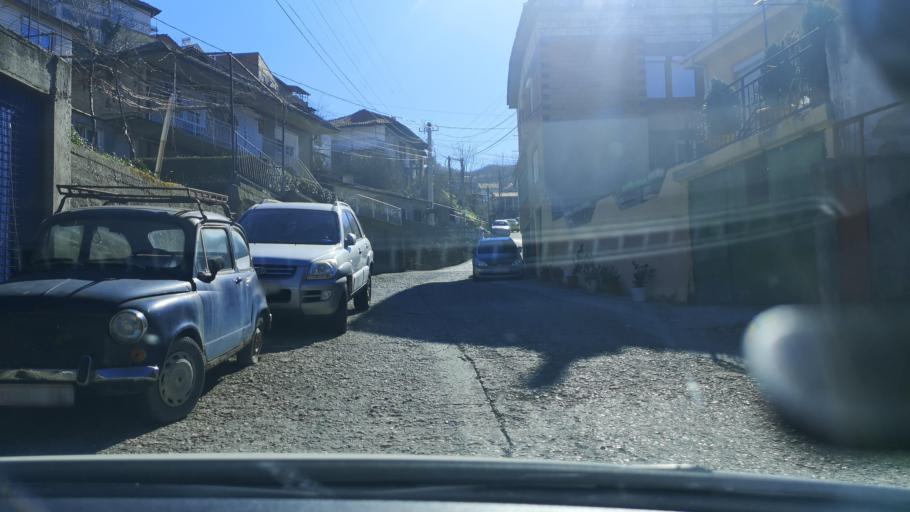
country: MK
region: Veles
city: Veles
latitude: 41.7134
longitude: 21.7769
